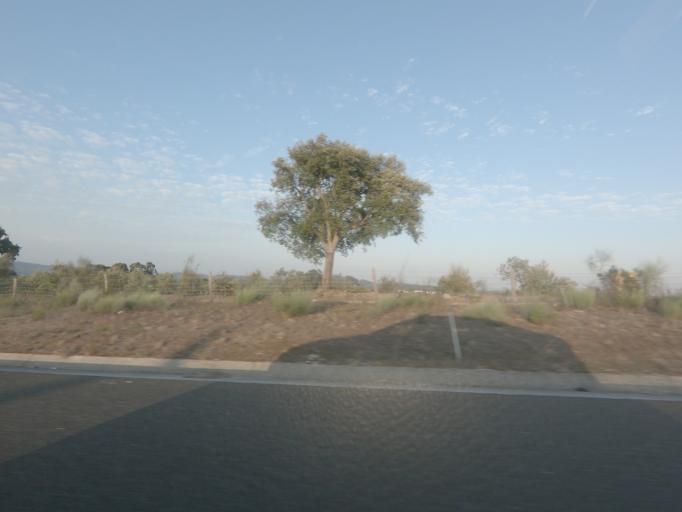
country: PT
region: Leiria
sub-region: Leiria
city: Santa Catarina da Serra
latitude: 39.6790
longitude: -8.6835
